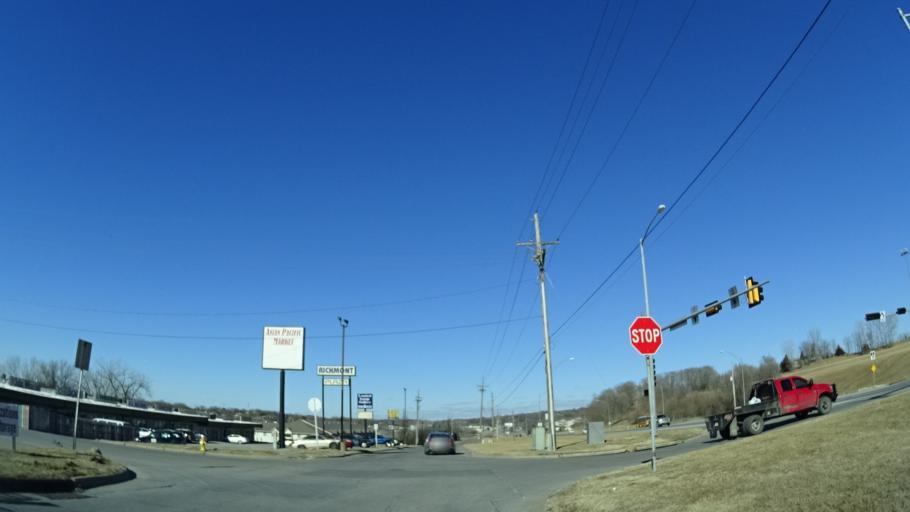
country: US
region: Nebraska
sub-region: Sarpy County
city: Offutt Air Force Base
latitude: 41.1524
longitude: -95.9276
